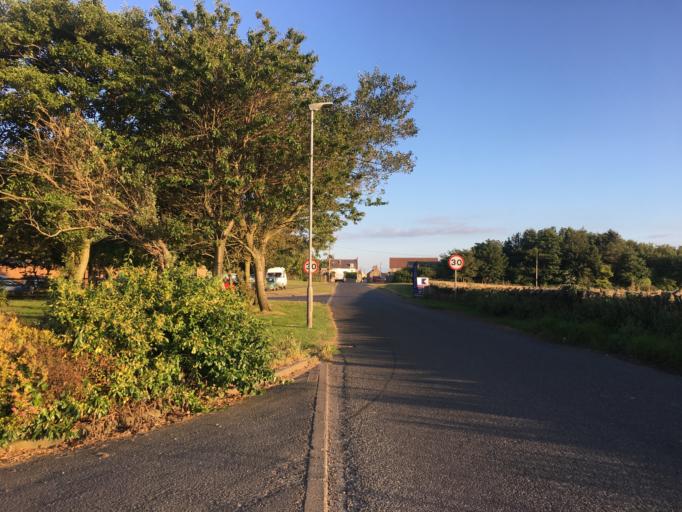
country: GB
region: England
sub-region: Northumberland
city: North Sunderland
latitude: 55.5789
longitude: -1.6681
